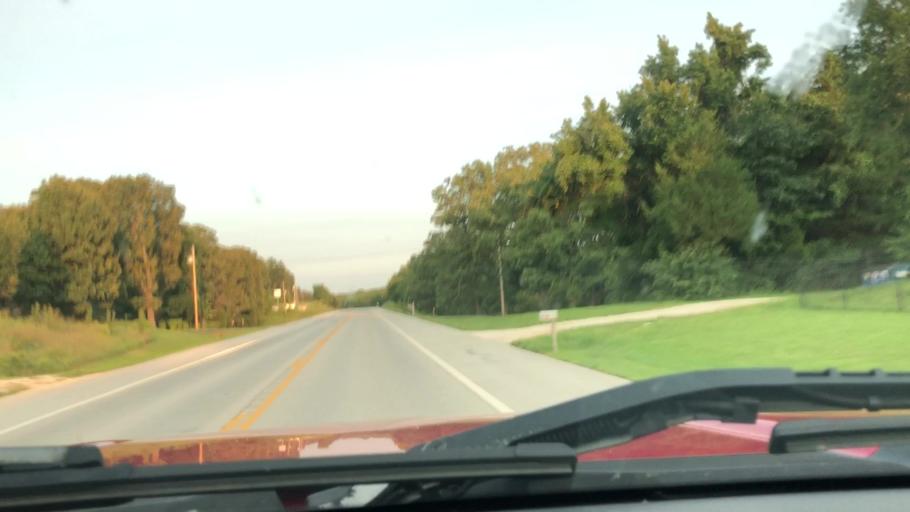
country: US
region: Missouri
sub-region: Jasper County
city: Duquesne
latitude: 36.9712
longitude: -94.4493
